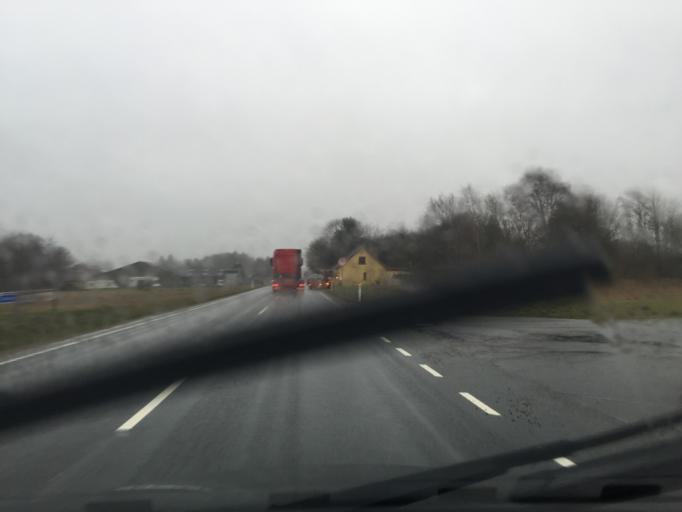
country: DK
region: South Denmark
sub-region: Vejle Kommune
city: Give
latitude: 55.9807
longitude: 9.2847
